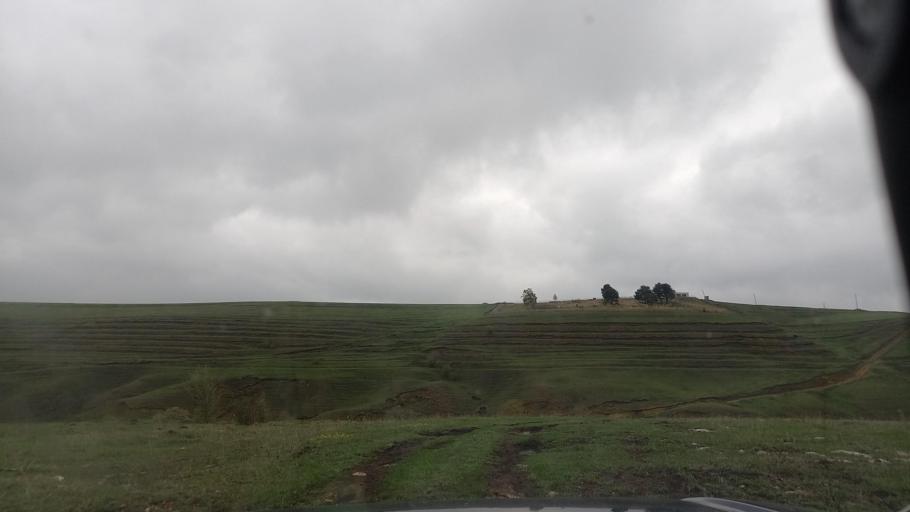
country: RU
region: Stavropol'skiy
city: Nezhinskiy
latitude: 43.8551
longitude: 42.6354
